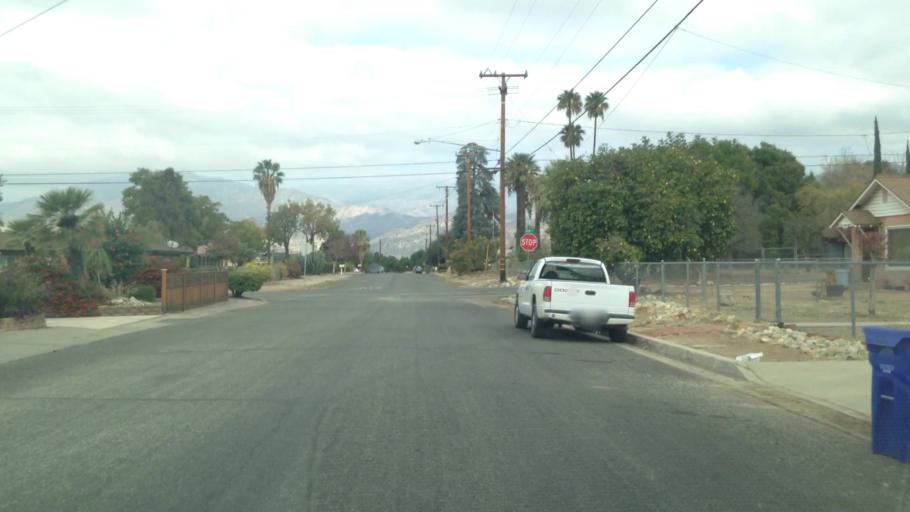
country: US
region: California
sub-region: San Bernardino County
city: Mentone
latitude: 34.0746
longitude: -117.1375
